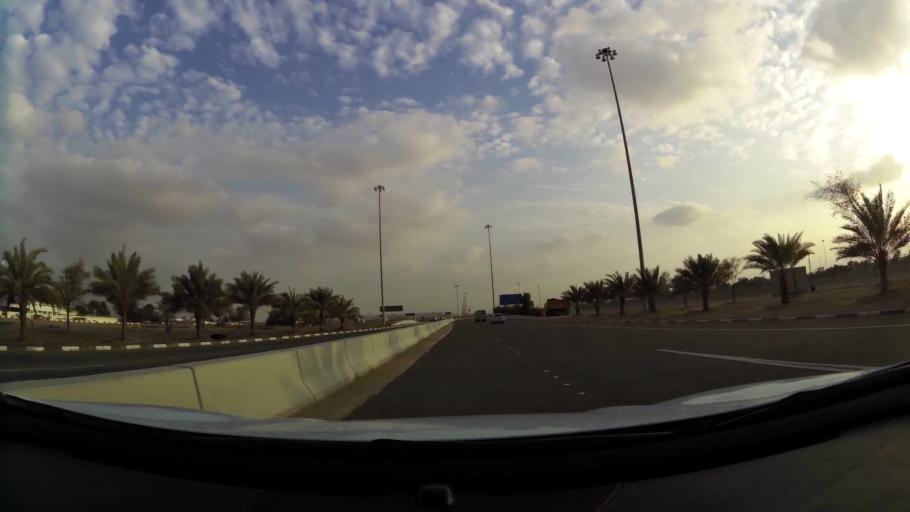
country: AE
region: Abu Dhabi
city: Abu Dhabi
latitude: 24.3714
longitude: 54.5278
